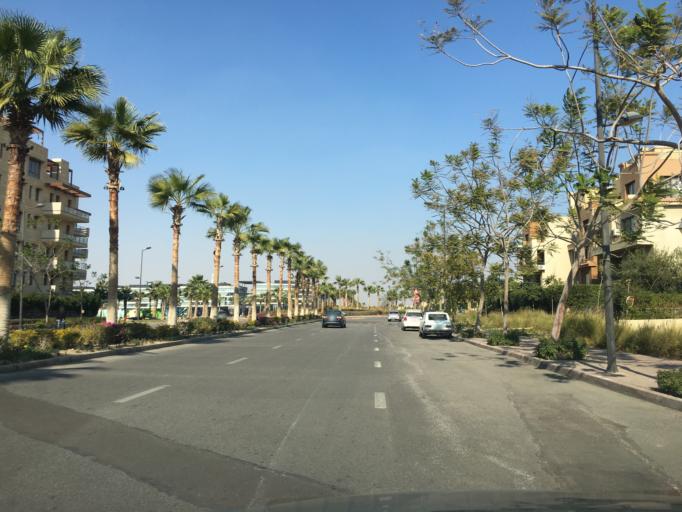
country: EG
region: Al Jizah
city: Awsim
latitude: 30.0666
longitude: 30.9469
